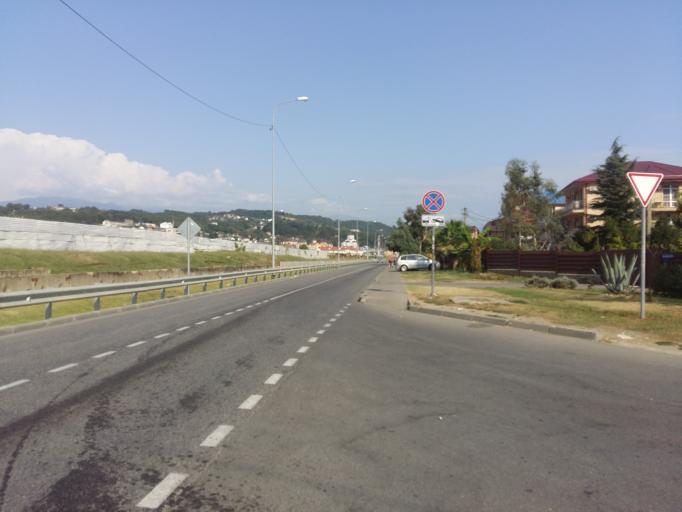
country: RU
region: Krasnodarskiy
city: Adler
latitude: 43.4152
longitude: 39.9580
